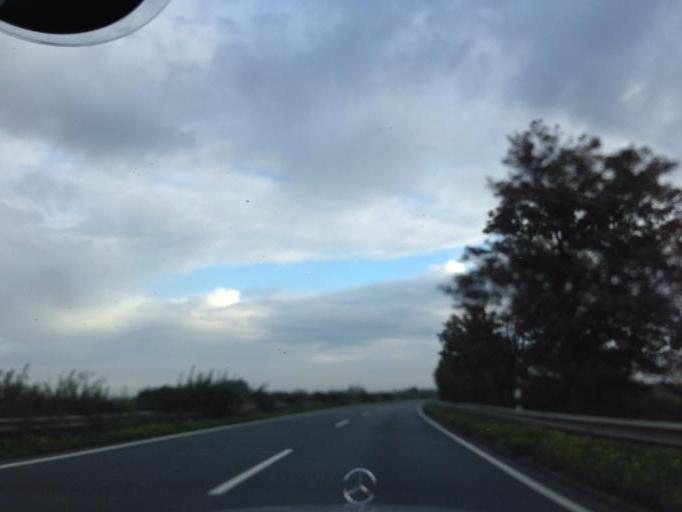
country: DE
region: Schleswig-Holstein
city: Grabau
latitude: 53.7992
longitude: 10.3147
